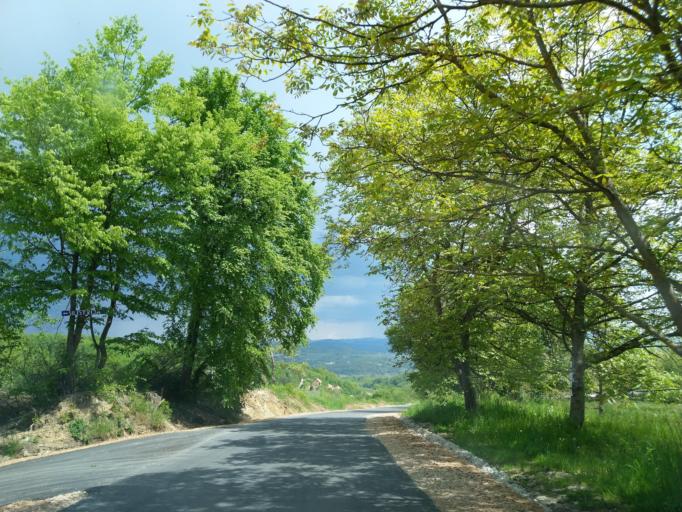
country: RS
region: Central Serbia
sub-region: Zlatiborski Okrug
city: Uzice
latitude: 43.8605
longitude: 19.9253
